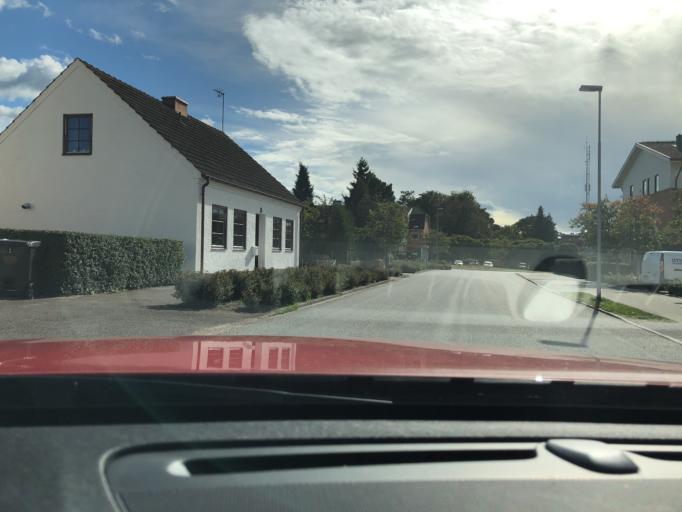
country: SE
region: Skane
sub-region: Sjobo Kommun
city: Sjoebo
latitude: 55.6343
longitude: 13.7039
